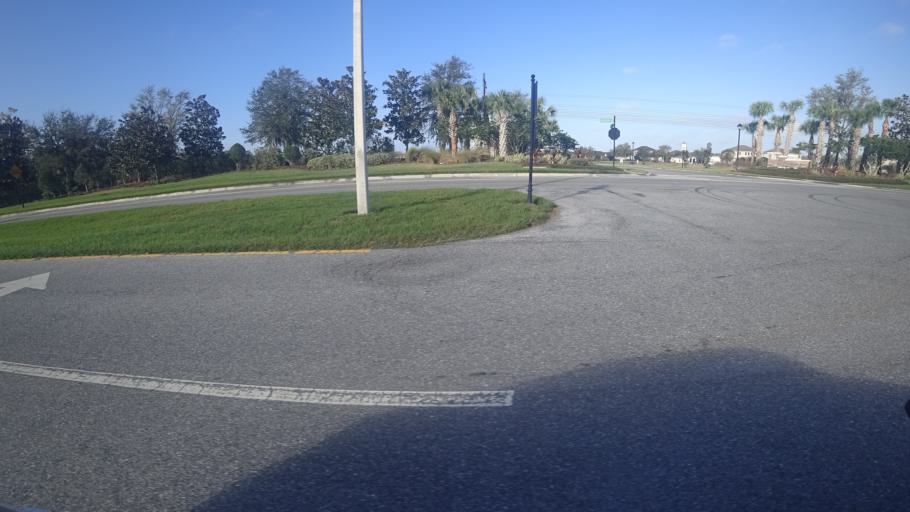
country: US
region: Florida
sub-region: Manatee County
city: Ellenton
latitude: 27.5589
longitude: -82.4580
